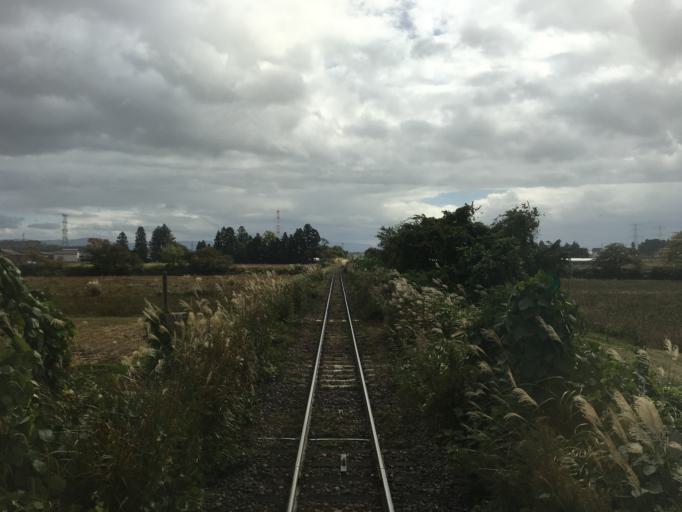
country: JP
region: Yamagata
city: Nagai
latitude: 38.0656
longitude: 140.0348
